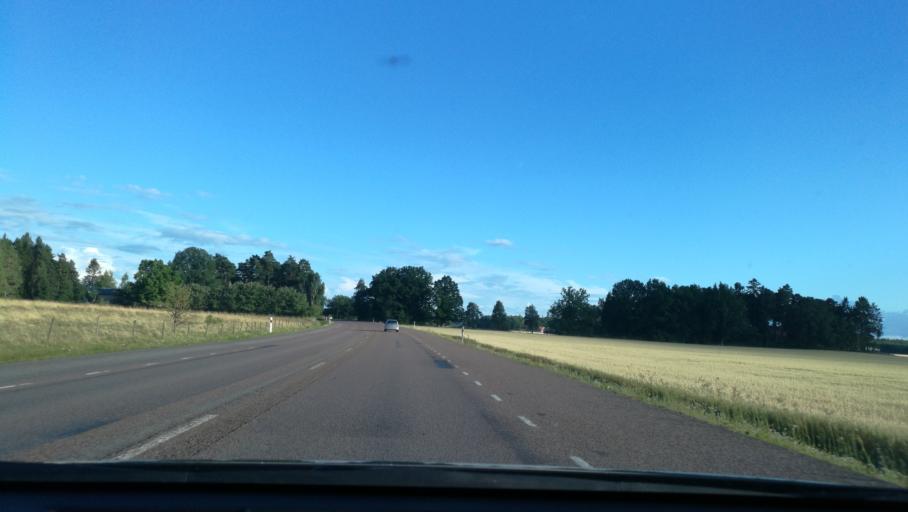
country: SE
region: Vaestmanland
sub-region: Kopings Kommun
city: Koping
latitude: 59.4692
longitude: 15.9918
